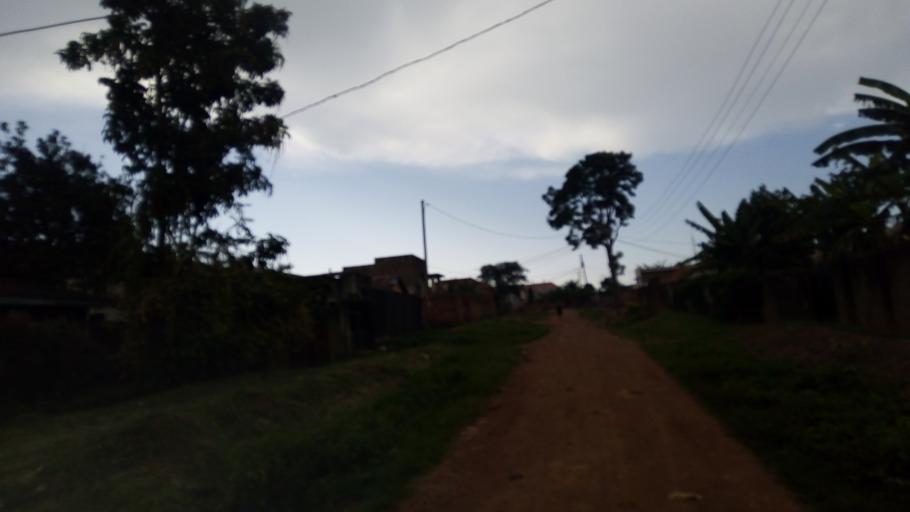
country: UG
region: Eastern Region
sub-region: Mbale District
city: Mbale
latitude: 1.0756
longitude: 34.1679
